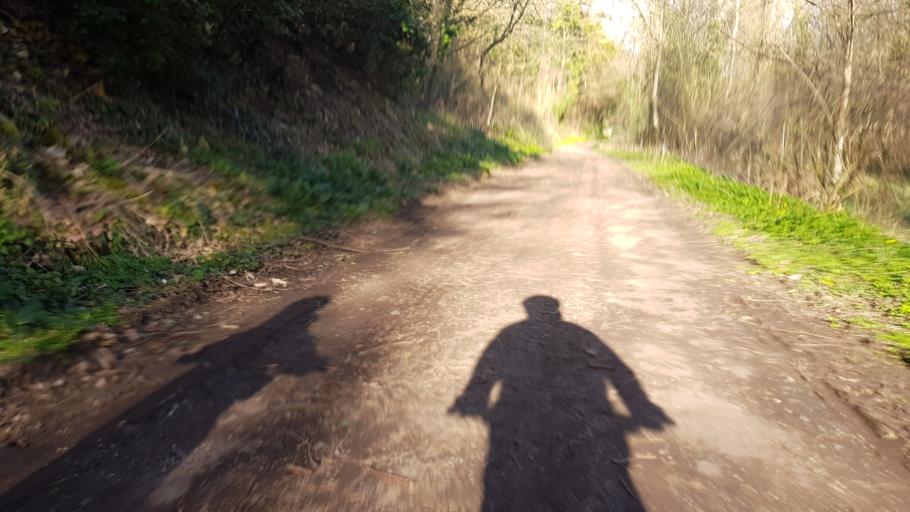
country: FR
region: Poitou-Charentes
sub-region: Departement de la Vienne
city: Migne-Auxances
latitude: 46.6305
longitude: 0.3243
